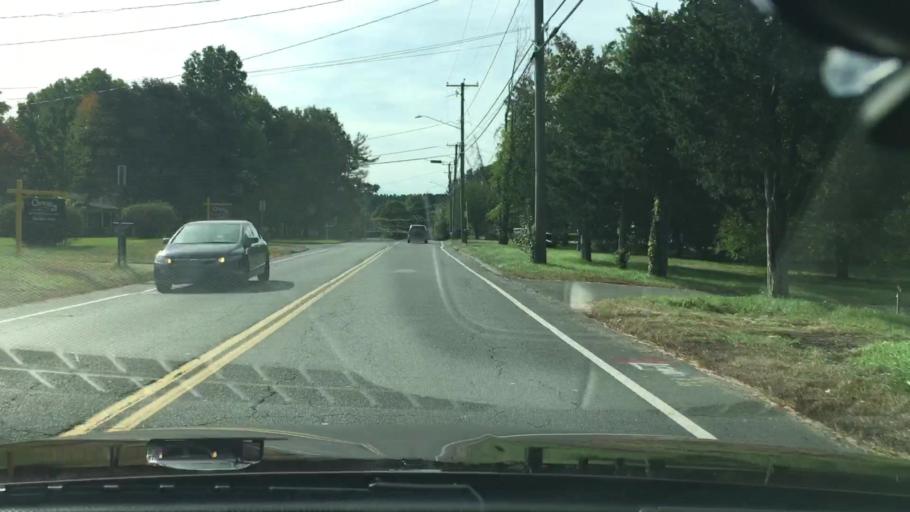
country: US
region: Connecticut
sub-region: Hartford County
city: Plainville
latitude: 41.6952
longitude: -72.8777
